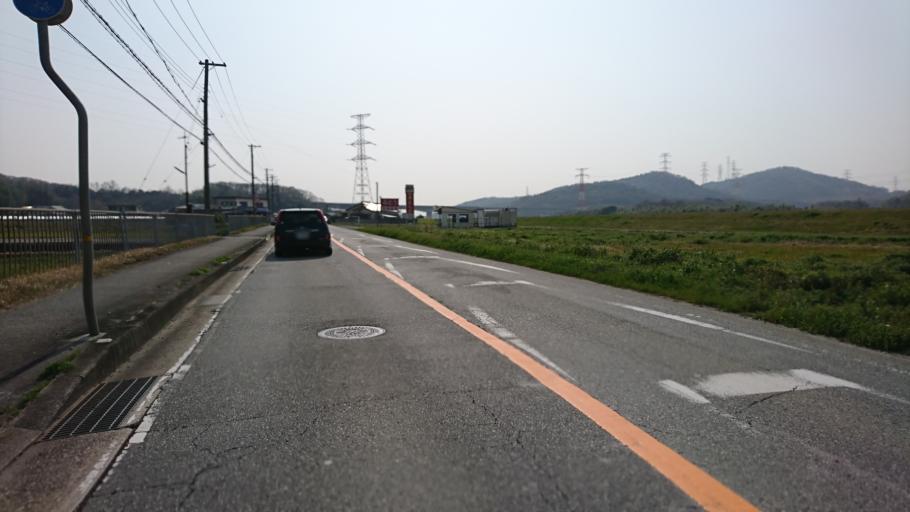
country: JP
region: Hyogo
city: Ono
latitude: 34.8145
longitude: 134.9371
